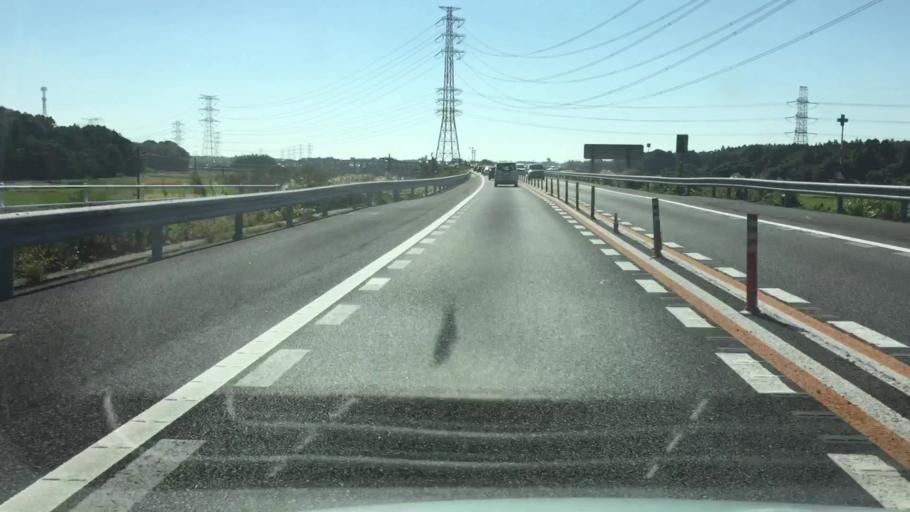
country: JP
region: Ibaraki
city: Ushiku
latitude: 36.0057
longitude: 140.1451
